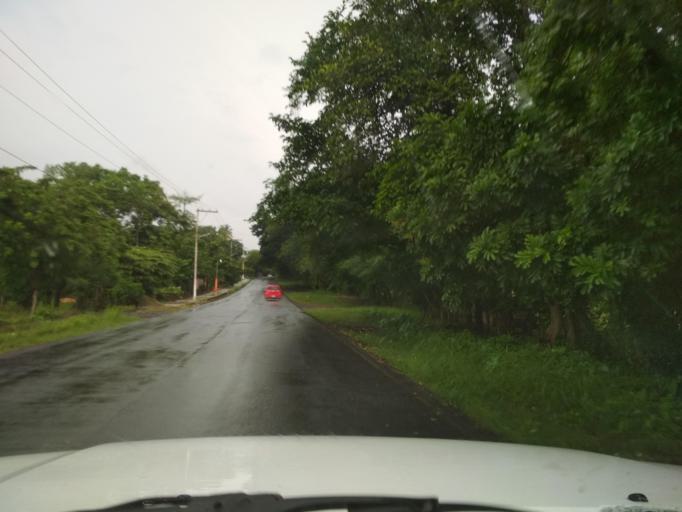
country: MX
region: Veracruz
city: Santiago Tuxtla
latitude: 18.4481
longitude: -95.3167
